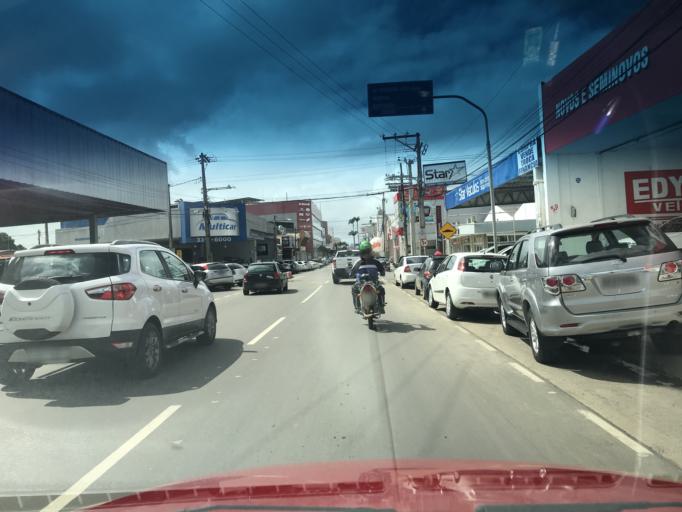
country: BR
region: Bahia
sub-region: Santo Antonio De Jesus
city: Santo Antonio de Jesus
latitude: -12.9663
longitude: -39.2700
